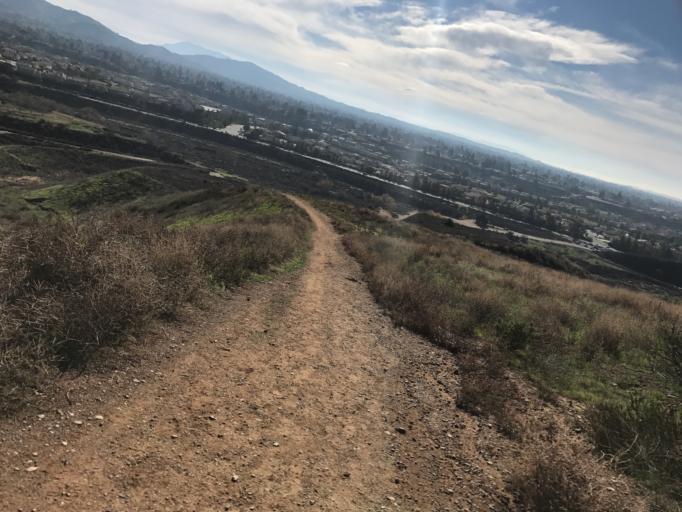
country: US
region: California
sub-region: San Bernardino County
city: Yucaipa
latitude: 34.0479
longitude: -117.0599
